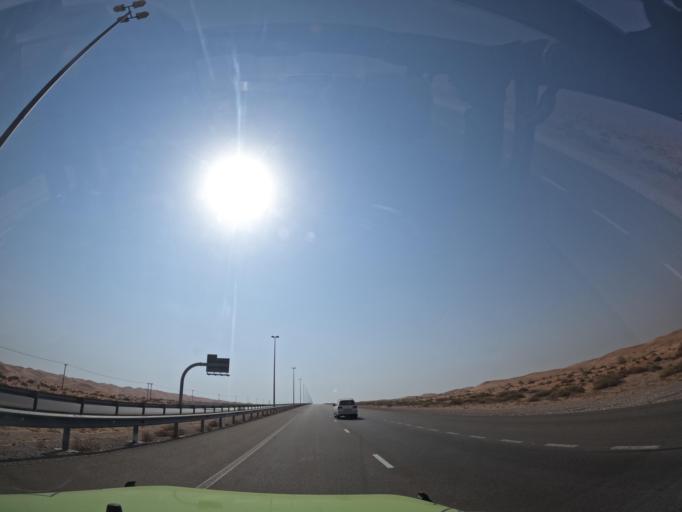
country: OM
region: Al Buraimi
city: Al Buraymi
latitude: 24.4334
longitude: 55.6739
